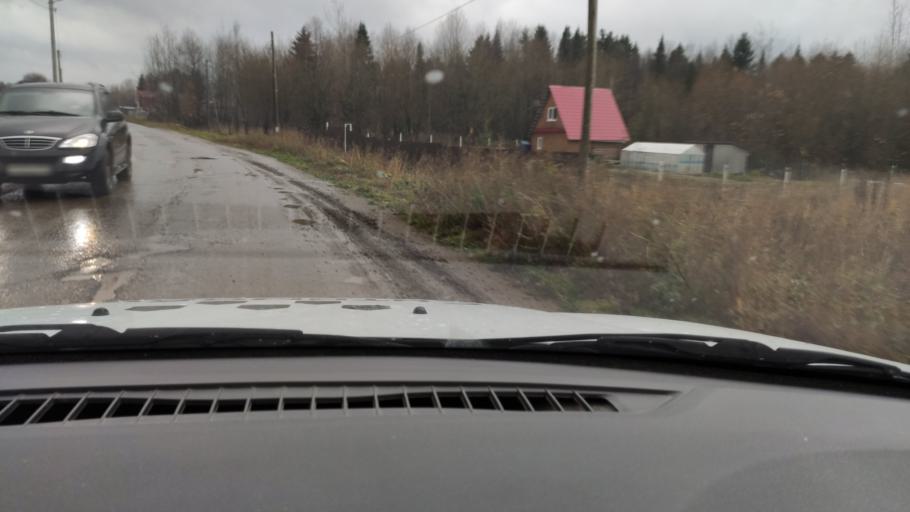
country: RU
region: Perm
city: Sylva
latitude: 58.0394
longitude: 56.7454
